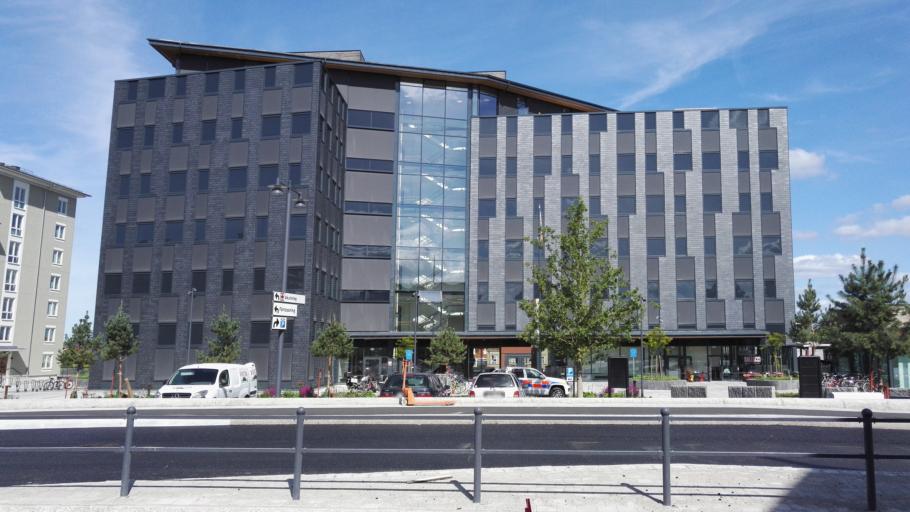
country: SE
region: Kronoberg
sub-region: Vaxjo Kommun
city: Vaexjoe
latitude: 56.8757
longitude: 14.8066
